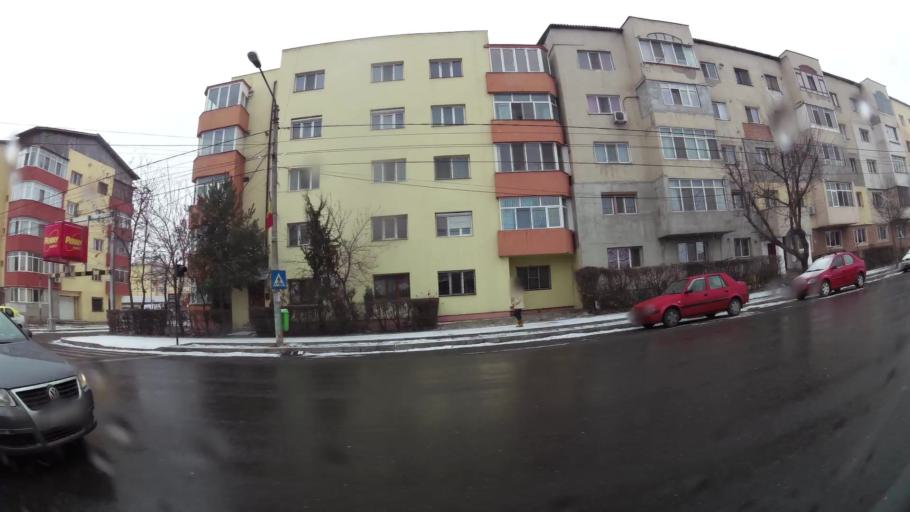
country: RO
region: Dambovita
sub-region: Comuna Ulmi
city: Ulmi
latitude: 44.9145
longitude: 25.4801
